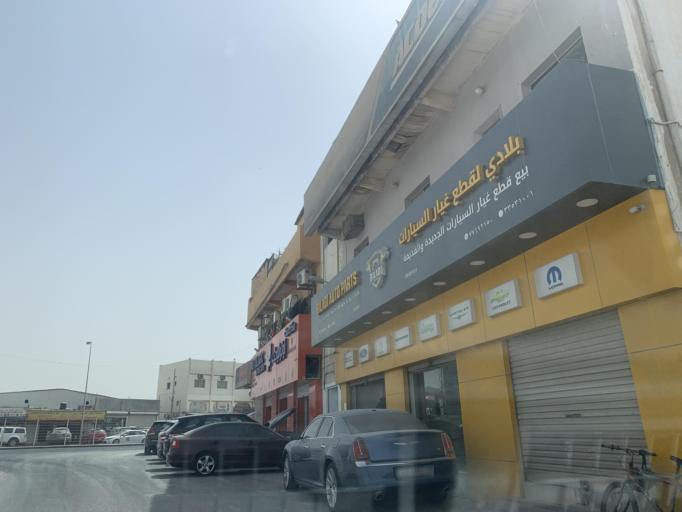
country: BH
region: Northern
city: Madinat `Isa
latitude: 26.1864
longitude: 50.5278
